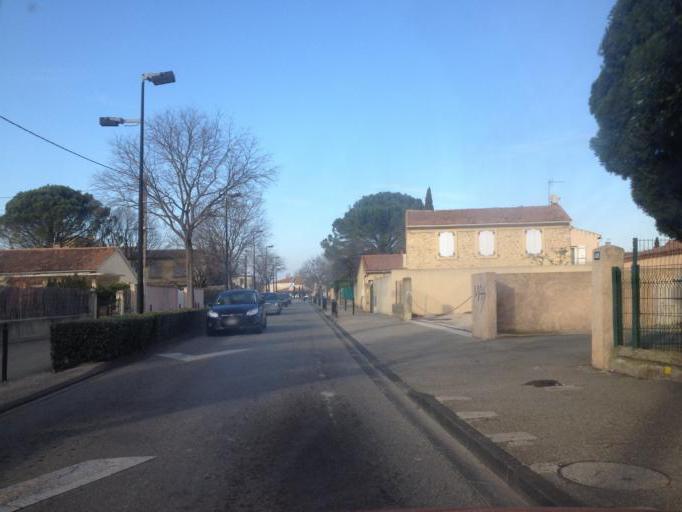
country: FR
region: Provence-Alpes-Cote d'Azur
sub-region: Departement du Vaucluse
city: Orange
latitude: 44.1427
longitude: 4.8016
